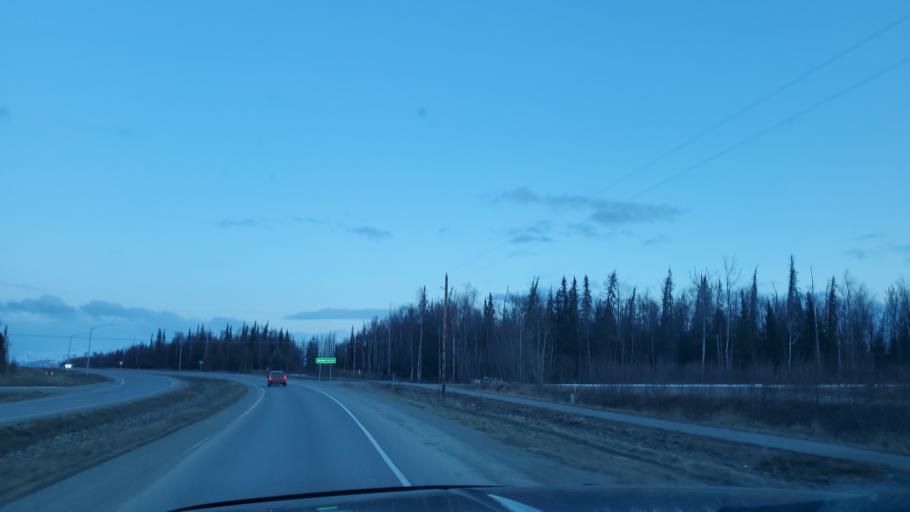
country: US
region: Alaska
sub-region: Matanuska-Susitna Borough
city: Wasilla
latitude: 61.5705
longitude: -149.4390
